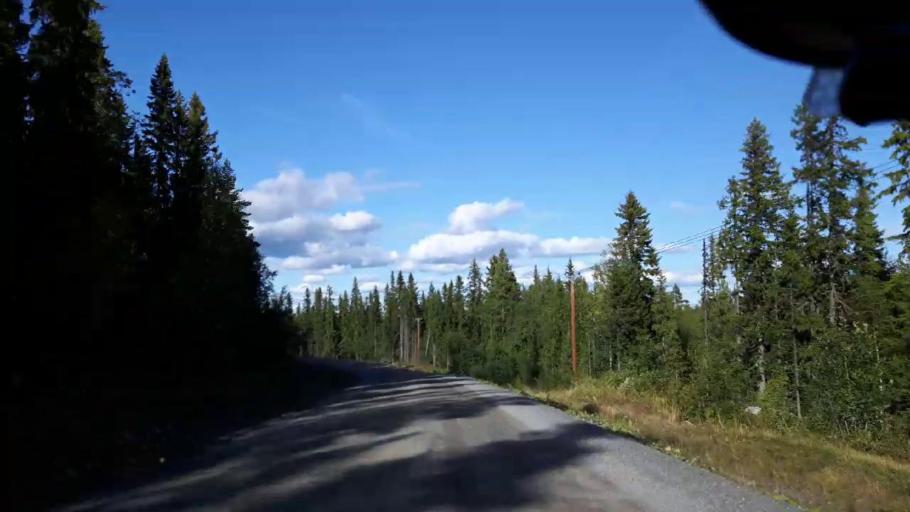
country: SE
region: Jaemtland
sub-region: Ragunda Kommun
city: Hammarstrand
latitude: 63.4290
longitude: 16.1798
